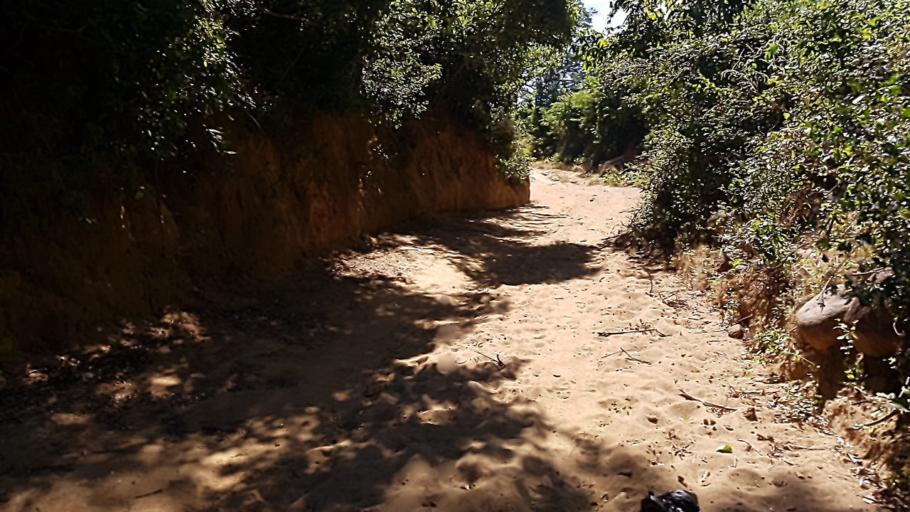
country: NI
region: Carazo
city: Santa Teresa
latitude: 11.6627
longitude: -86.1745
